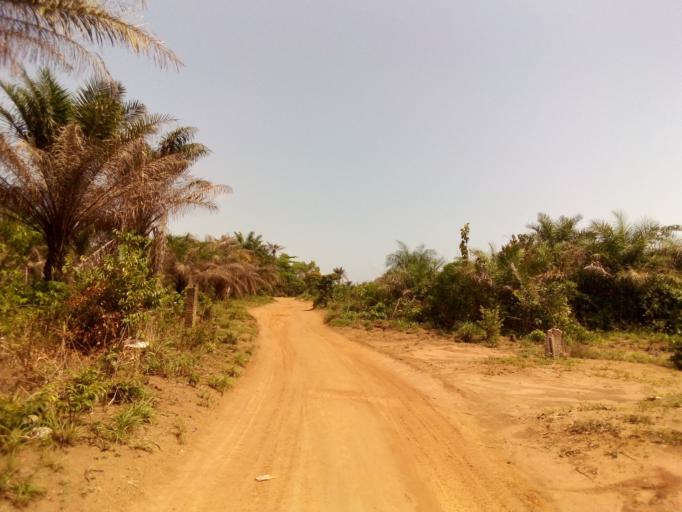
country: SL
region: Western Area
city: Waterloo
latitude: 8.3440
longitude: -13.0126
